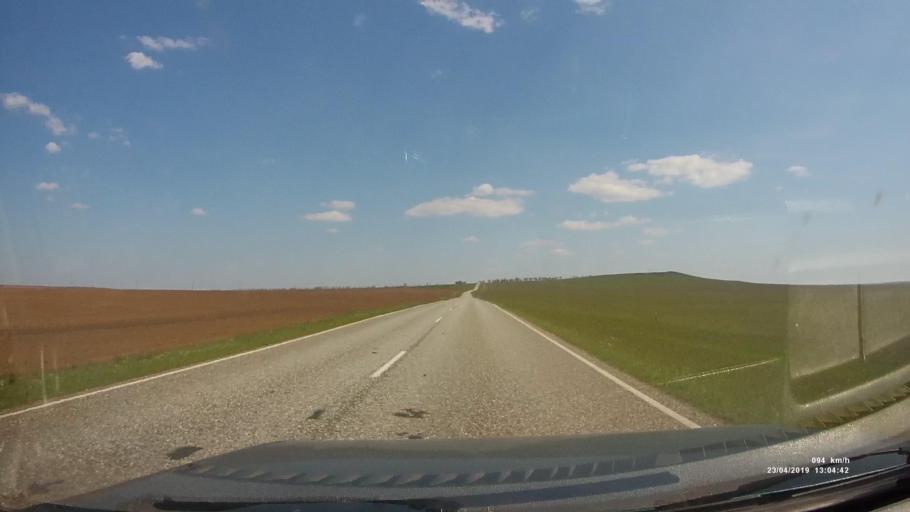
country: RU
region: Kalmykiya
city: Yashalta
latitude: 46.5933
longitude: 42.7083
